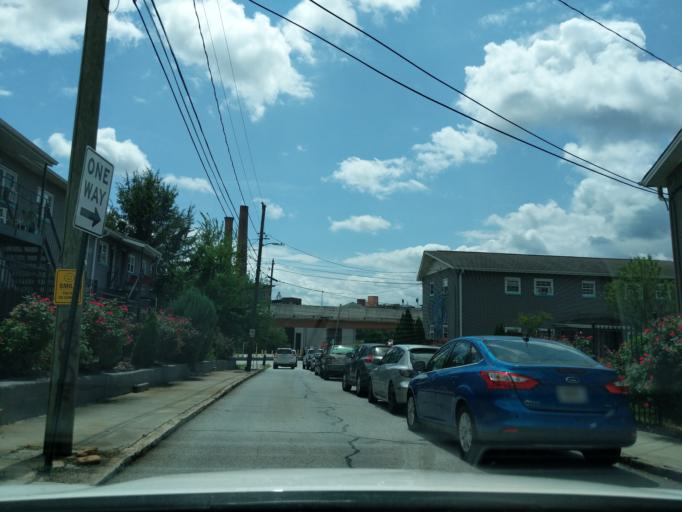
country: US
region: Georgia
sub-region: Fulton County
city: Atlanta
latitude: 33.7529
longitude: -84.3689
